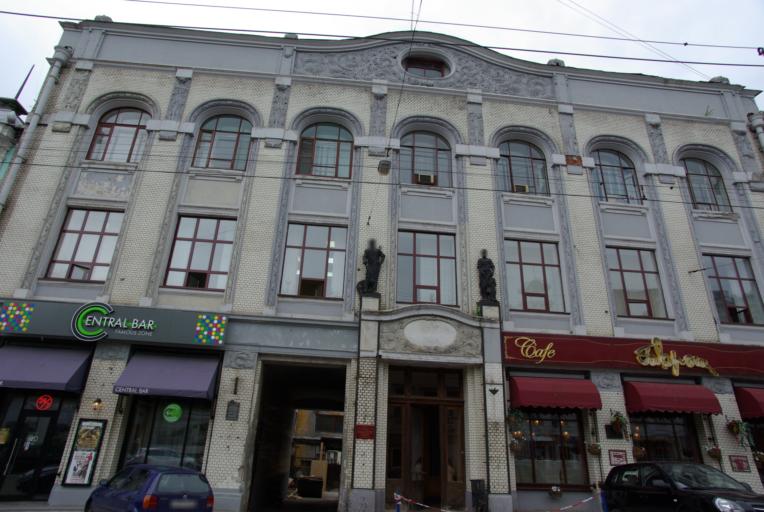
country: RU
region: Nizjnij Novgorod
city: Nizhniy Novgorod
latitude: 56.3284
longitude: 43.9881
